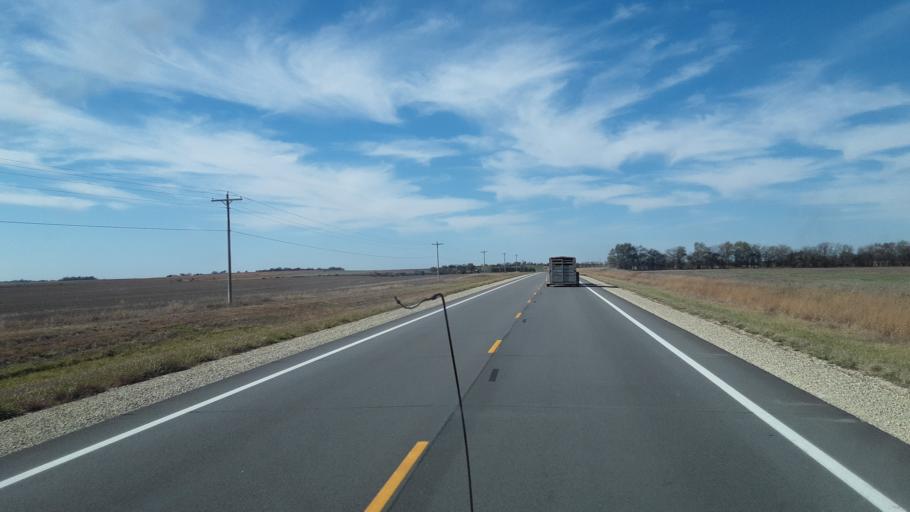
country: US
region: Kansas
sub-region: Marion County
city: Marion
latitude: 38.3629
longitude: -96.9218
